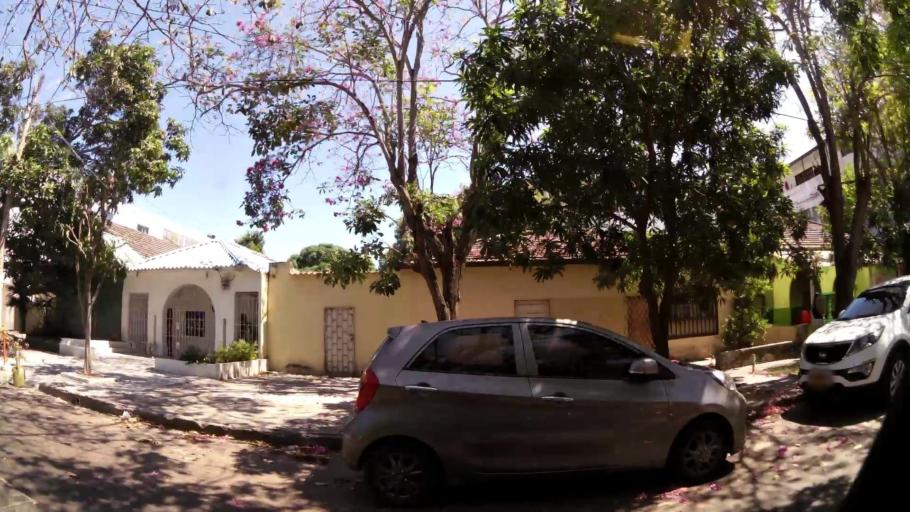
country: CO
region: Atlantico
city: Barranquilla
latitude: 10.9862
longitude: -74.7956
